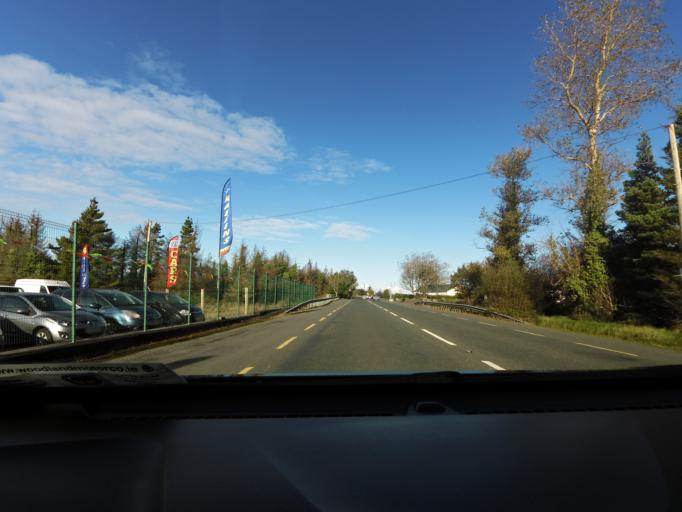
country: IE
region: Connaught
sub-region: County Galway
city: Moycullen
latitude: 53.4509
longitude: -9.0928
